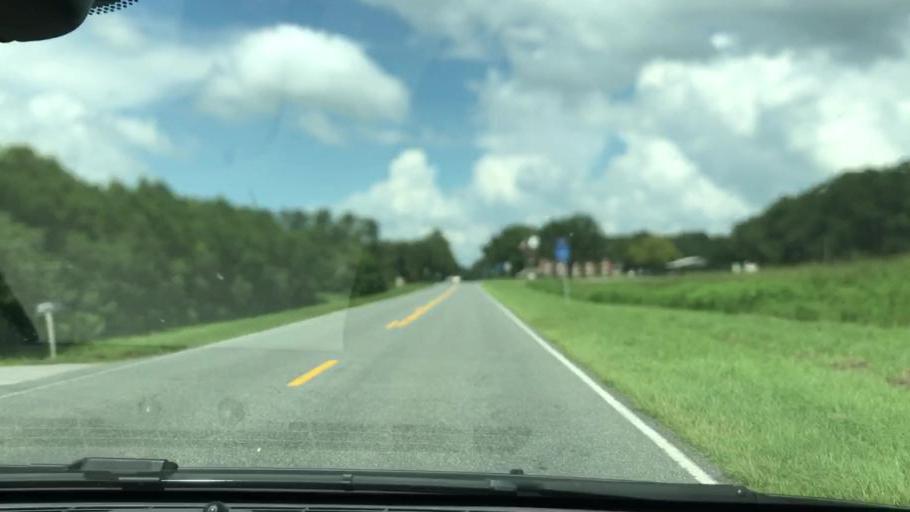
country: US
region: Florida
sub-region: Jackson County
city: Malone
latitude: 30.9209
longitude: -85.1187
